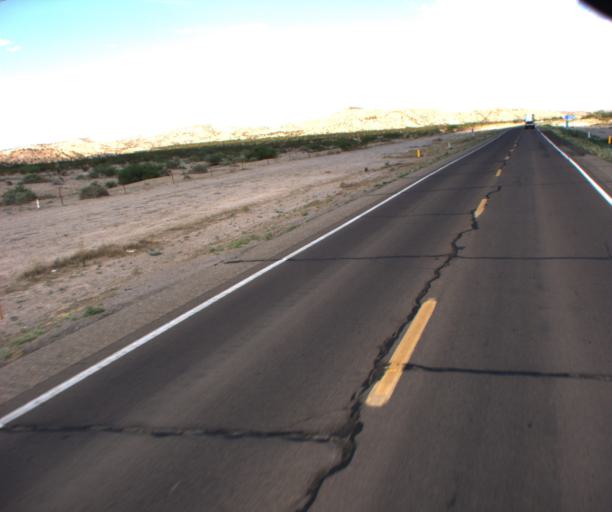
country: US
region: Arizona
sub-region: Greenlee County
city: Clifton
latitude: 32.7511
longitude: -109.1168
